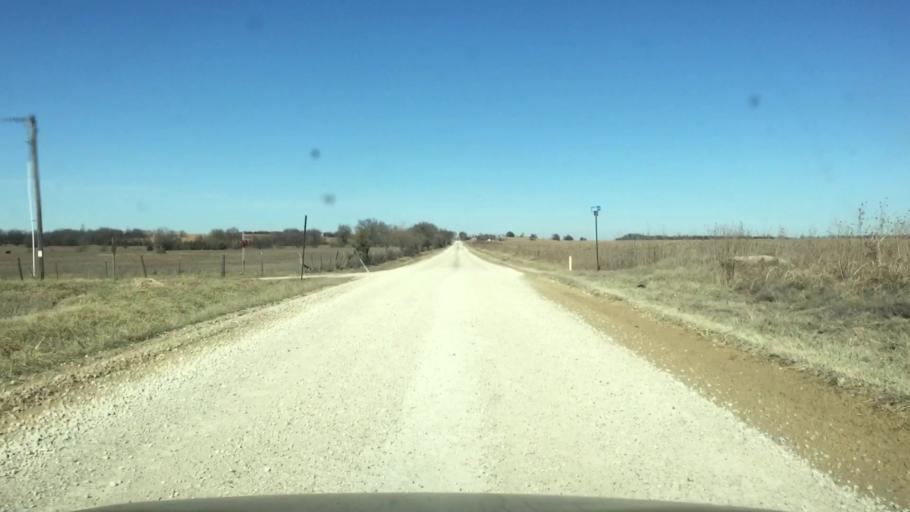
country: US
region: Kansas
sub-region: Allen County
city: Iola
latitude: 37.8634
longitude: -95.3912
